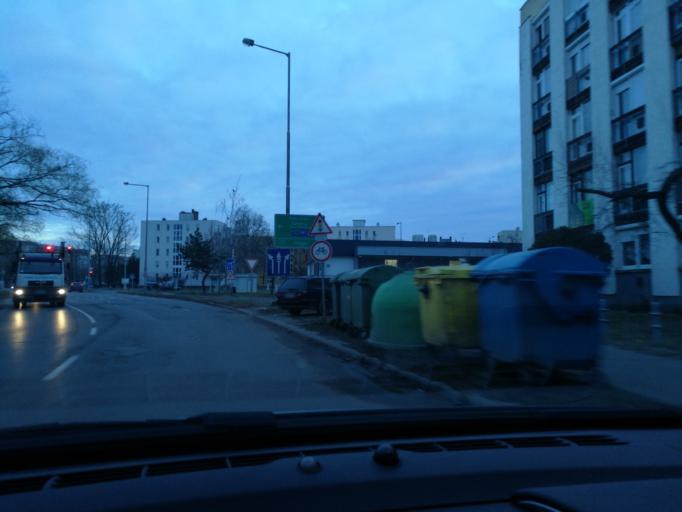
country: HU
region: Szabolcs-Szatmar-Bereg
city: Nyiregyhaza
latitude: 47.9665
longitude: 21.7098
